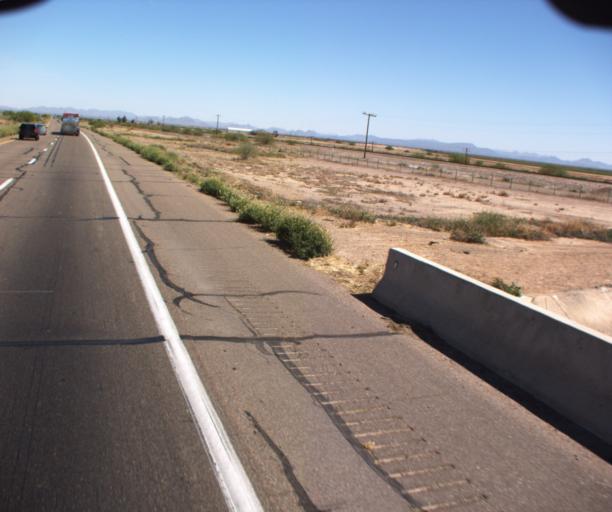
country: US
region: Arizona
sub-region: Maricopa County
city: Gila Bend
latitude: 32.9280
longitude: -112.8356
